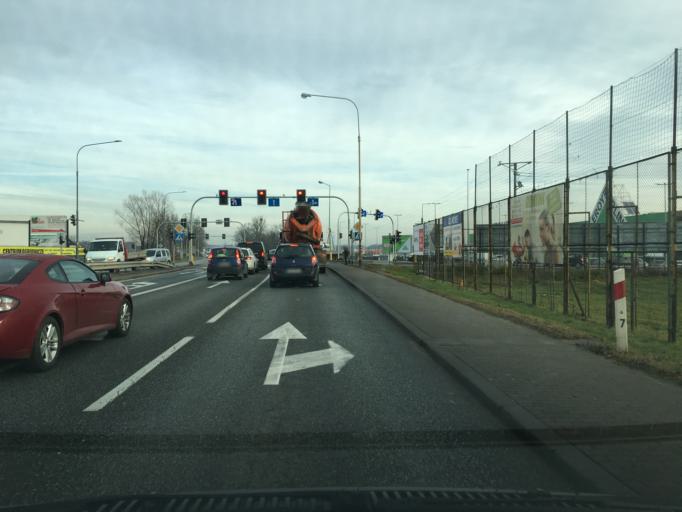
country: PL
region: Lower Silesian Voivodeship
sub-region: Powiat wroclawski
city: Mirkow
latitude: 51.1668
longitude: 17.1629
